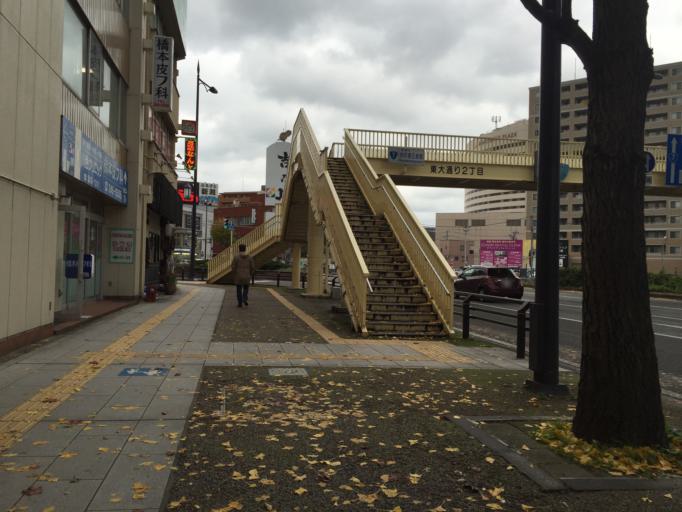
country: JP
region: Niigata
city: Niigata-shi
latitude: 37.9162
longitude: 139.0592
